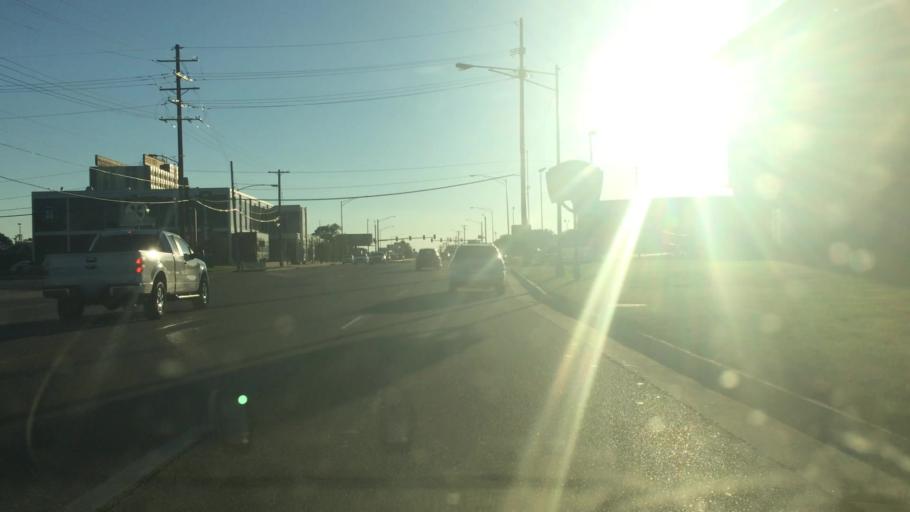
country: US
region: Missouri
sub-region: Greene County
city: Springfield
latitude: 37.1817
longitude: -93.2596
